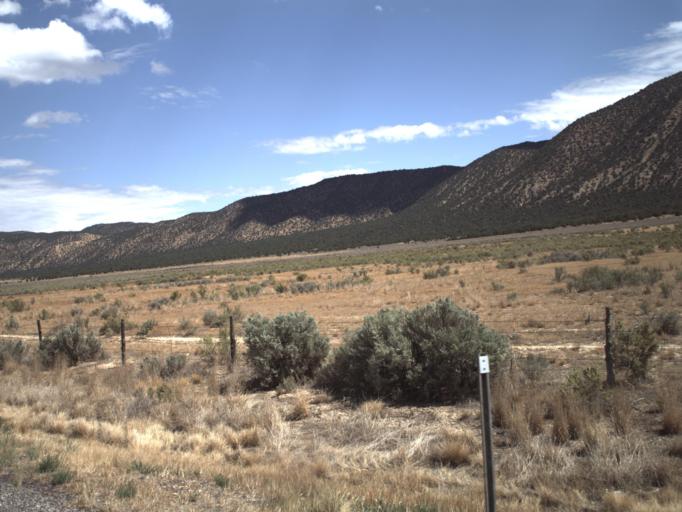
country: US
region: Utah
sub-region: Sevier County
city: Aurora
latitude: 39.0608
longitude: -112.0421
